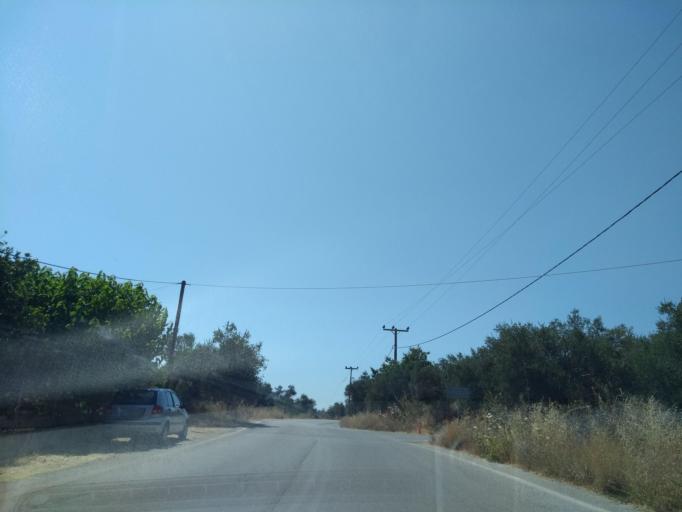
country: GR
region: Crete
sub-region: Nomos Chanias
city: Georgioupolis
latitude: 35.3786
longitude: 24.2449
